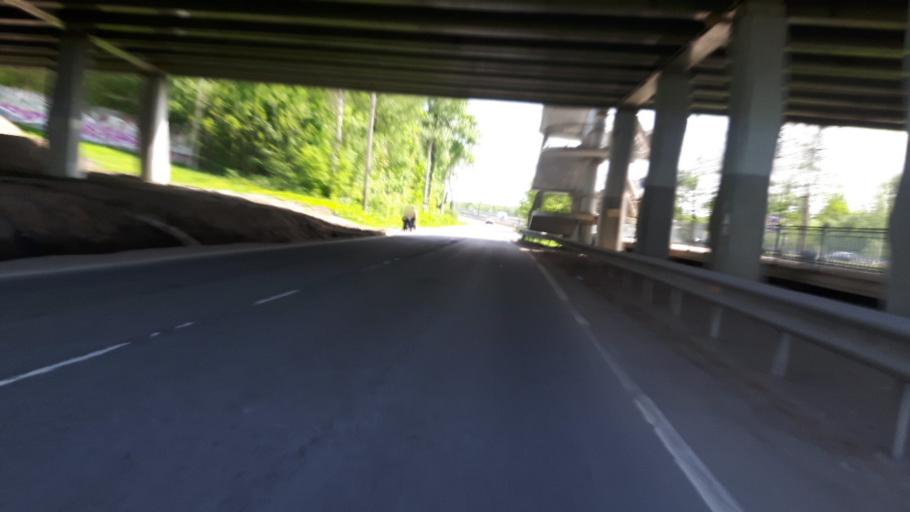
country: RU
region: Leningrad
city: Gorskaya
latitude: 60.0391
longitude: 29.9775
